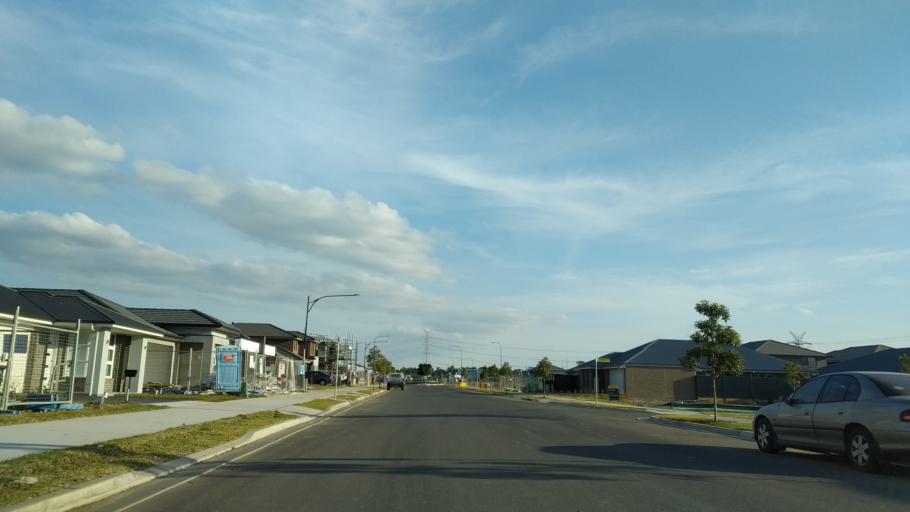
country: AU
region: New South Wales
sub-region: Penrith Municipality
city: Werrington County
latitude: -33.7331
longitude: 150.7551
